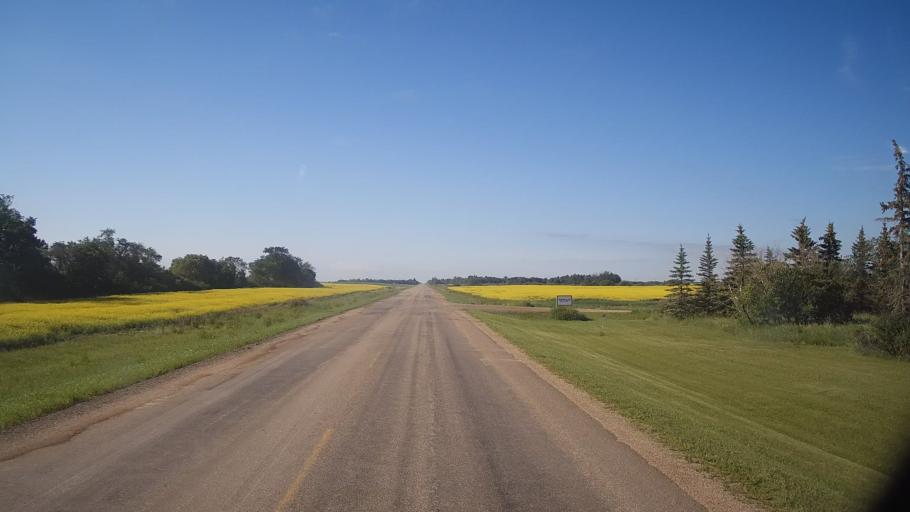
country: CA
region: Saskatchewan
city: Watrous
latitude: 51.8151
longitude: -105.2866
